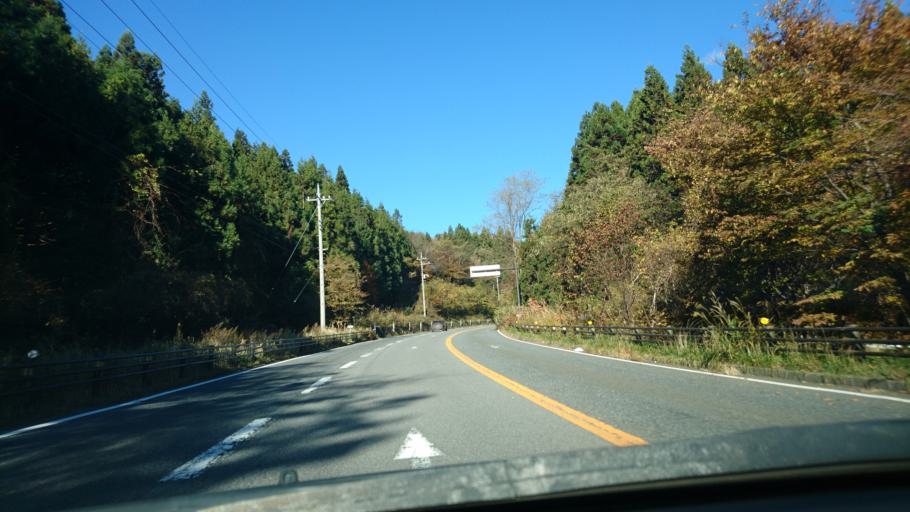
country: JP
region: Nagano
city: Saku
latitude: 36.3133
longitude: 138.6549
